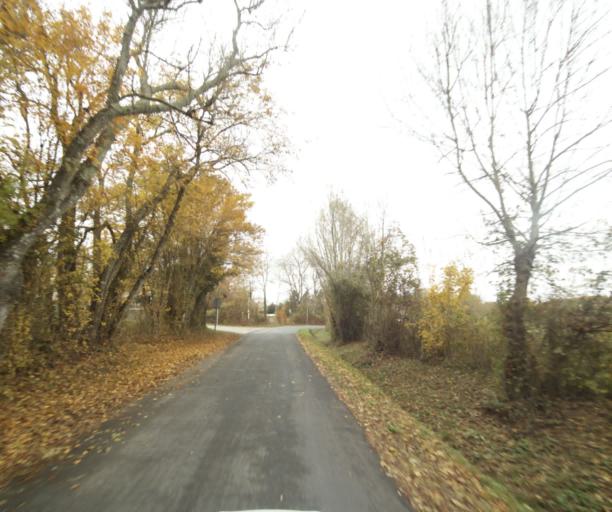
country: FR
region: Poitou-Charentes
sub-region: Departement de la Charente-Maritime
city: Saintes
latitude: 45.7613
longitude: -0.6268
